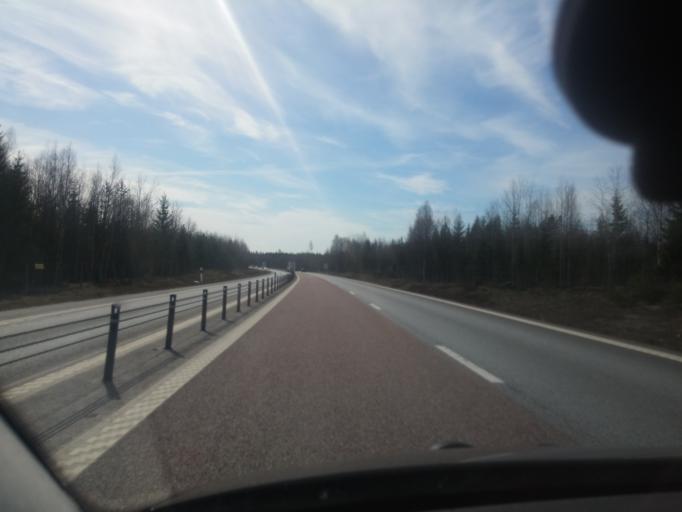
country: SE
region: Gaevleborg
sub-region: Gavle Kommun
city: Gavle
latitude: 60.7807
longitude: 17.0725
